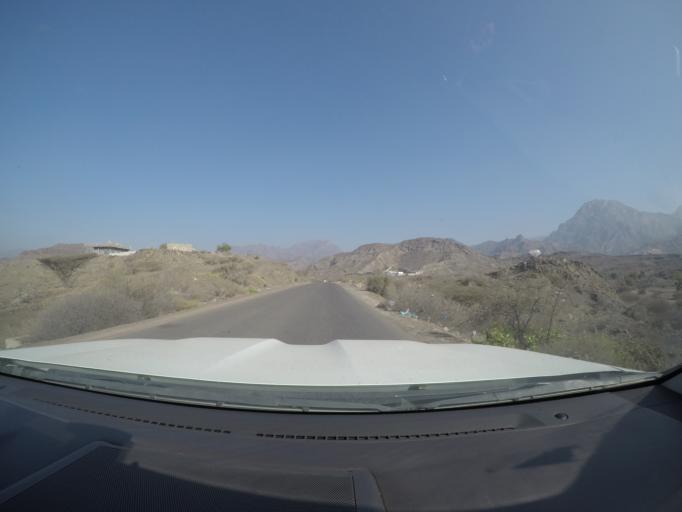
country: YE
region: Lahij
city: Habil ar Raydah
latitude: 13.6530
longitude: 44.8458
